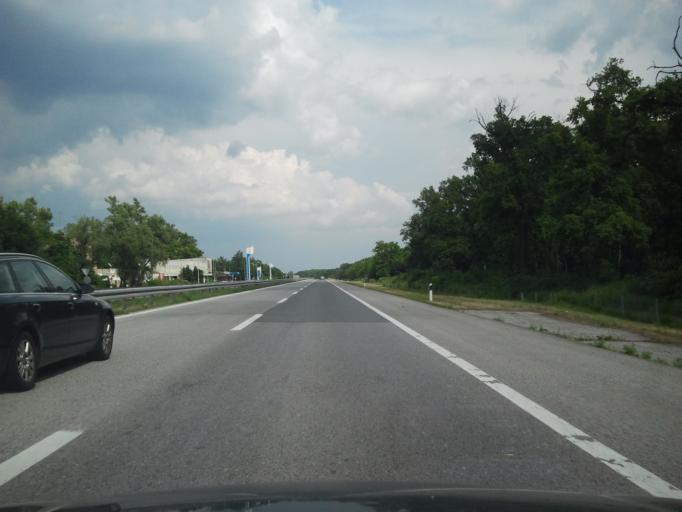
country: RS
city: Visnjicevo
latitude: 45.0419
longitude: 19.2583
